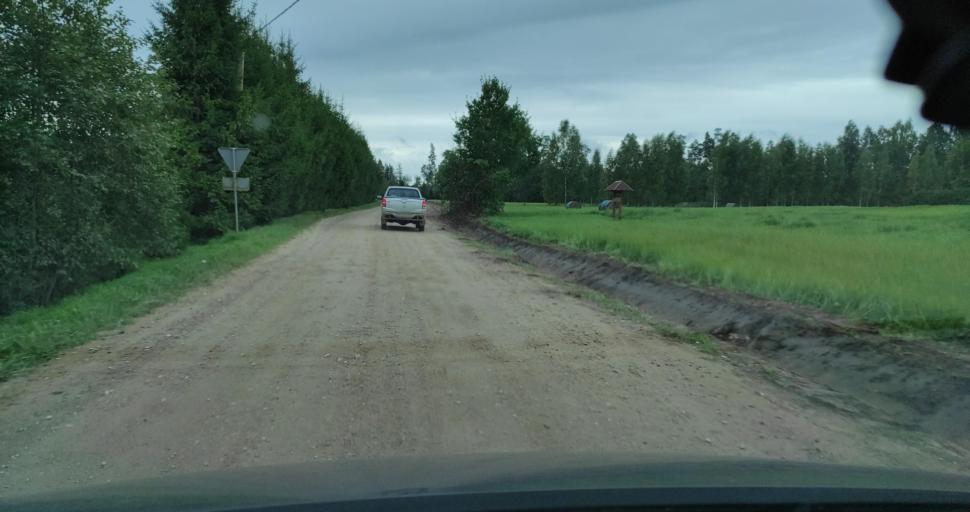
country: LV
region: Talsu Rajons
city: Stende
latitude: 57.0474
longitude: 22.3035
